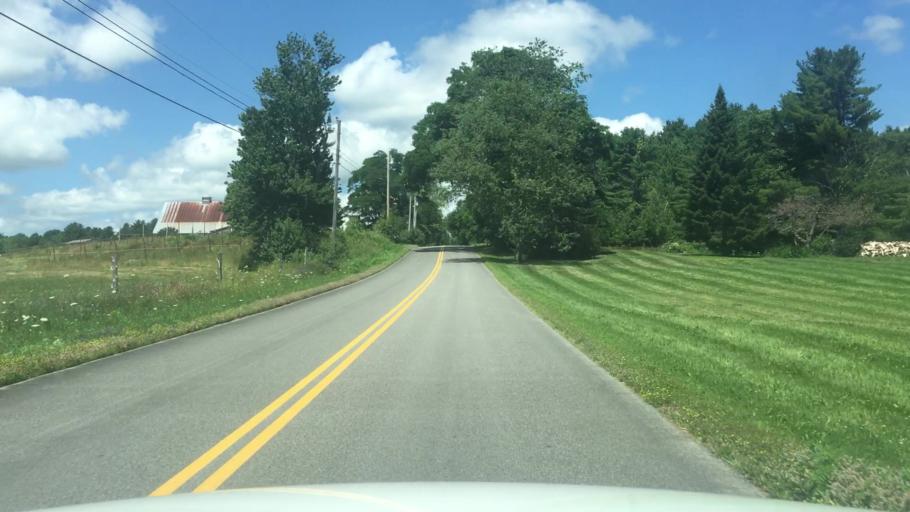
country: US
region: Maine
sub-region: Waldo County
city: Belfast
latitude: 44.4099
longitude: -69.0361
